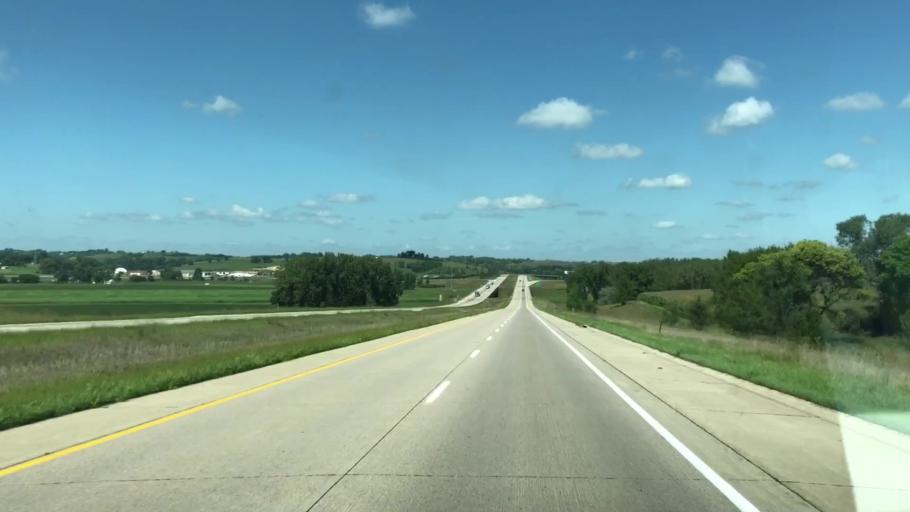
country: US
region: Iowa
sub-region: Woodbury County
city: Sioux City
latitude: 42.5393
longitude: -96.3394
